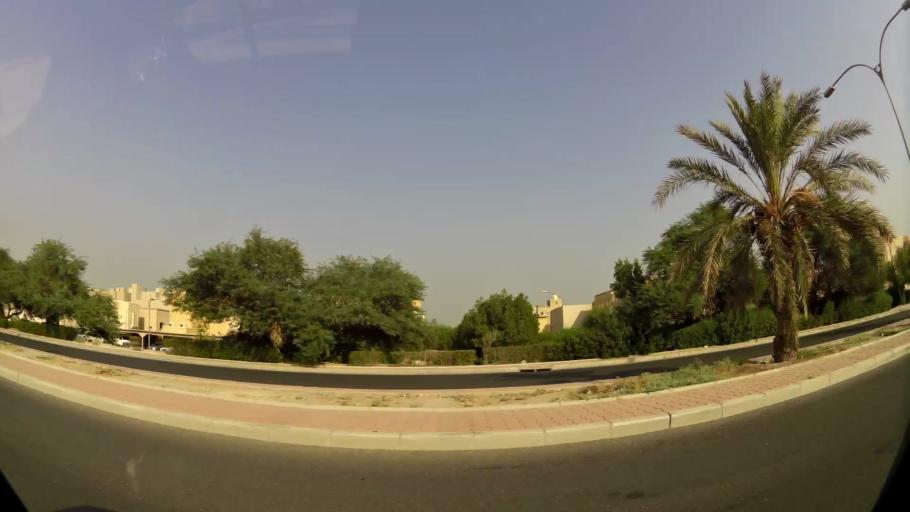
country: KW
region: Al Ahmadi
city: Ar Riqqah
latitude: 29.1304
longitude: 48.1036
